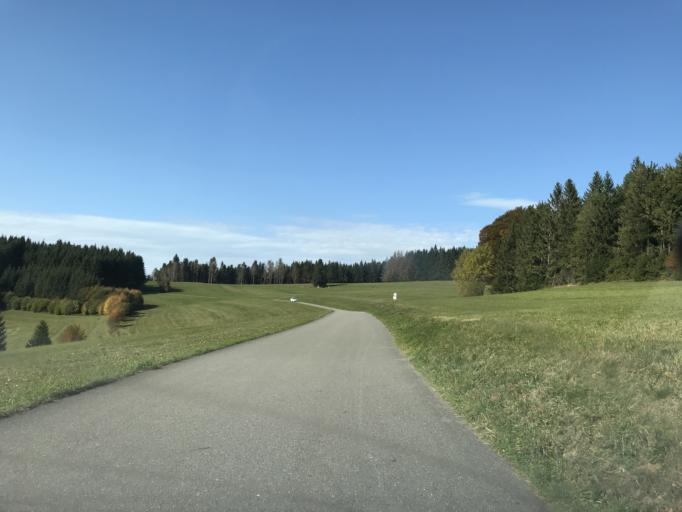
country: DE
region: Baden-Wuerttemberg
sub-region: Freiburg Region
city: Herrischried
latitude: 47.6747
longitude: 7.9809
